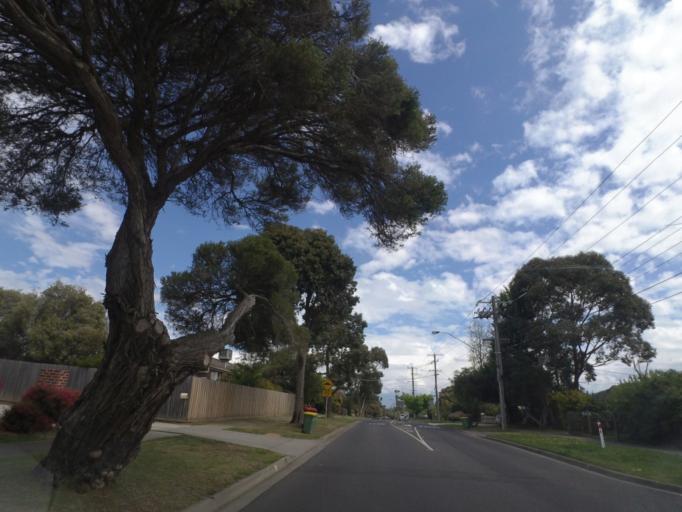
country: AU
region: Victoria
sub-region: Knox
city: Boronia
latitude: -37.8764
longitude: 145.2699
